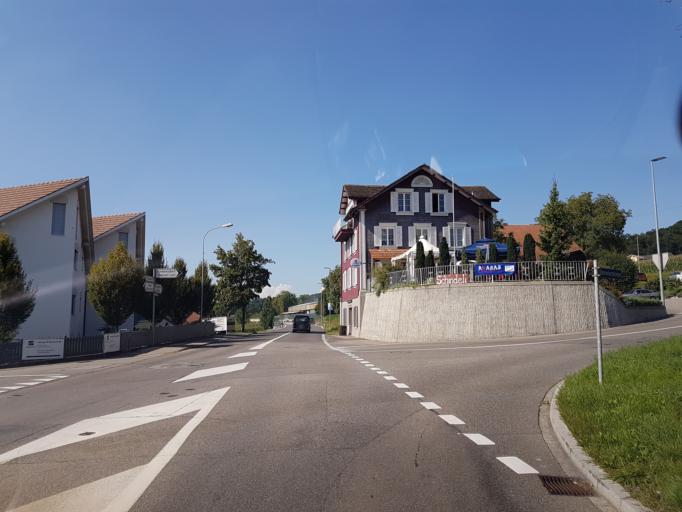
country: CH
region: Aargau
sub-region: Bezirk Bremgarten
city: Unterlunkhofen
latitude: 47.3238
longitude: 8.3793
